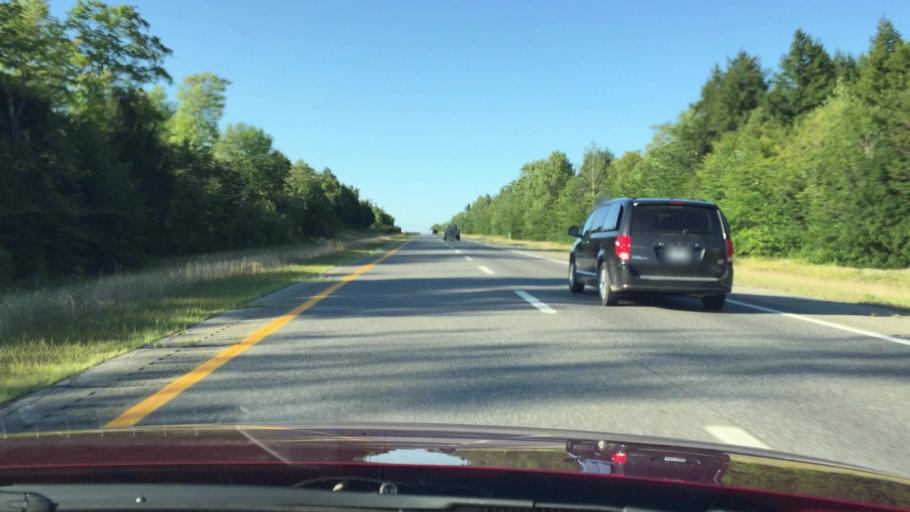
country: US
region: Maine
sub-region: Penobscot County
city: Lincoln
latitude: 45.4145
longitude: -68.5928
